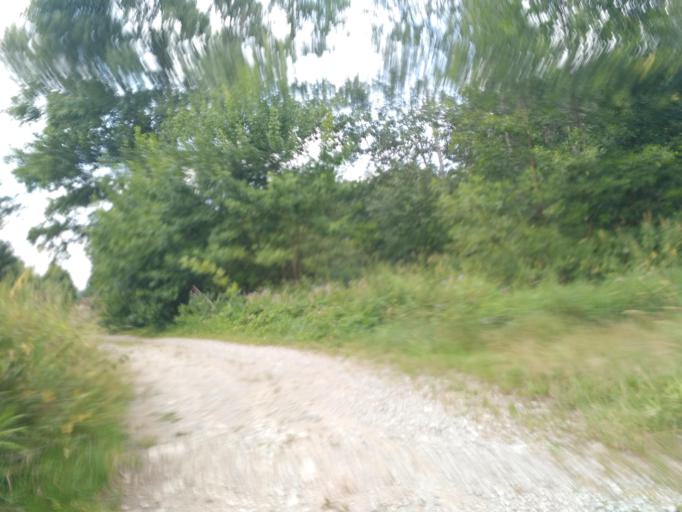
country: PL
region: Subcarpathian Voivodeship
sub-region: Powiat krosnienski
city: Rymanow
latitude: 49.5906
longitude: 21.8409
